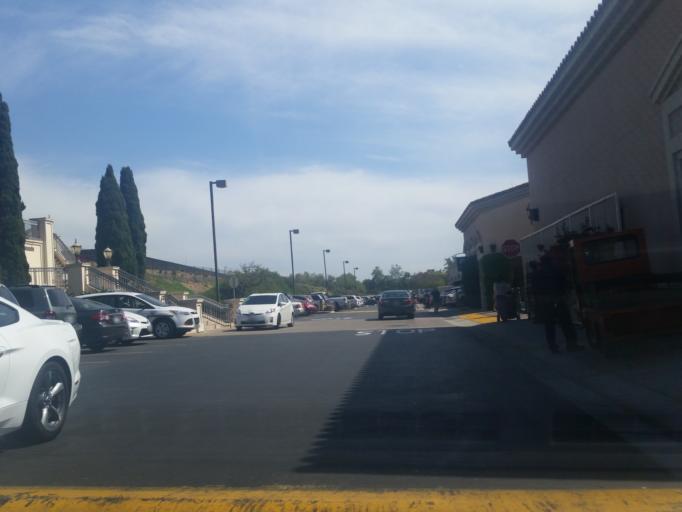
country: US
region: California
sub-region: San Diego County
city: Carlsbad
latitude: 33.1270
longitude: -117.3205
